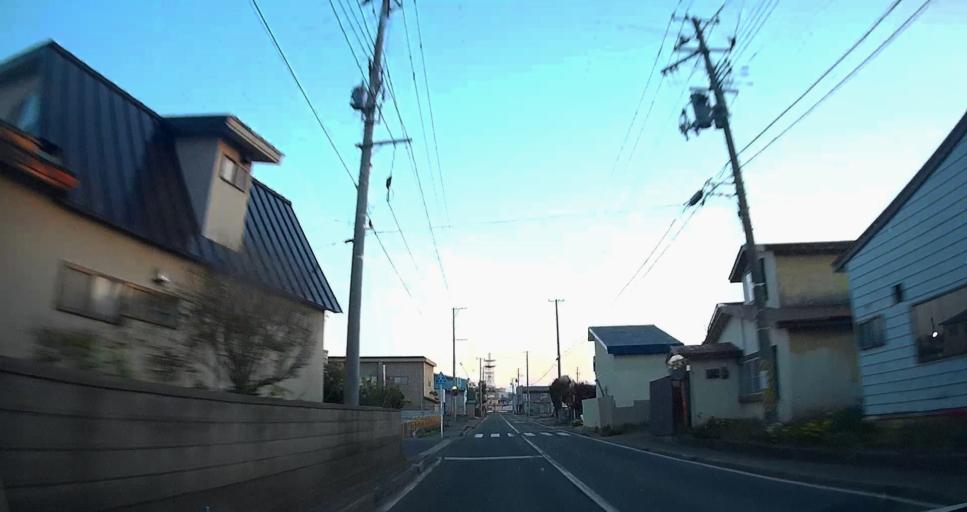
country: JP
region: Aomori
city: Misawa
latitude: 40.8698
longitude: 141.1312
